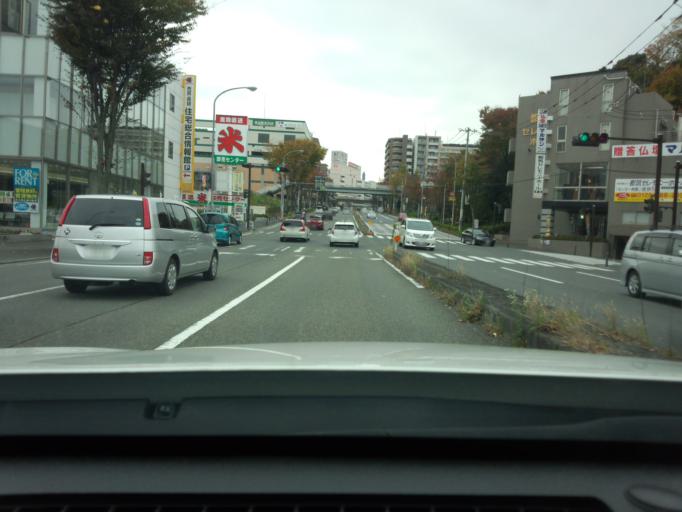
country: JP
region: Tokyo
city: Chofugaoka
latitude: 35.5491
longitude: 139.5740
